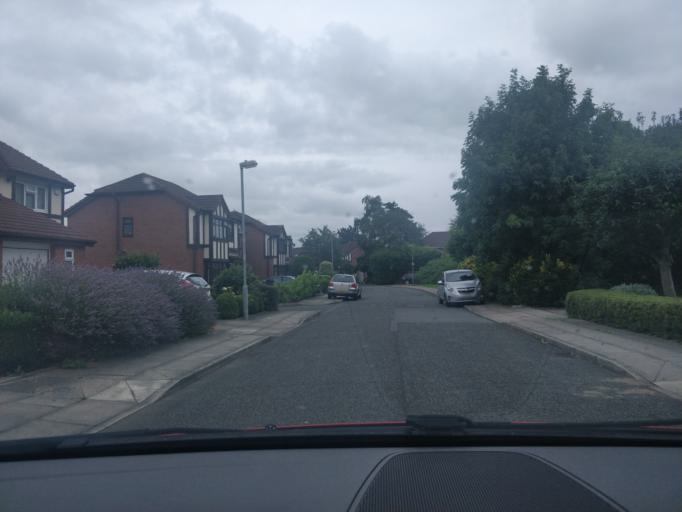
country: GB
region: England
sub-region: Sefton
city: Southport
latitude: 53.6359
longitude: -2.9845
